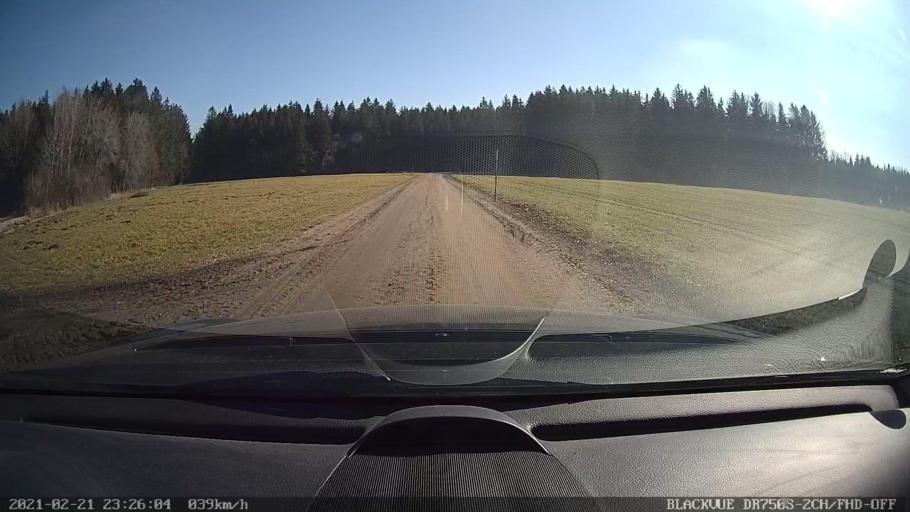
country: DE
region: Bavaria
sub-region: Upper Bavaria
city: Schonstett
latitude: 48.0016
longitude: 12.2227
